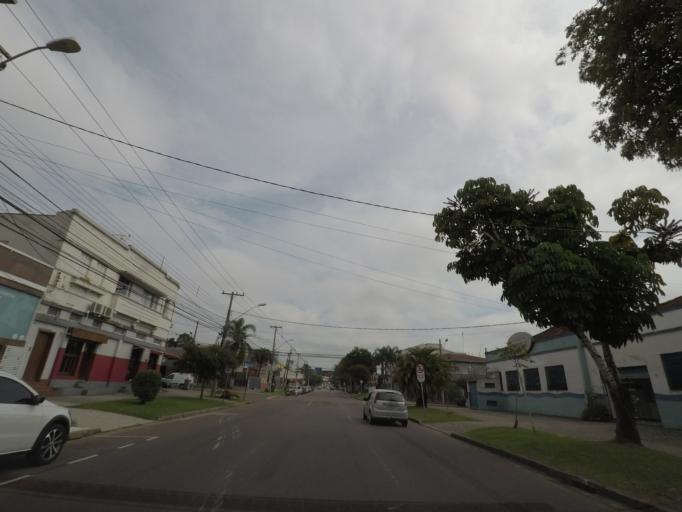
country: BR
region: Parana
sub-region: Curitiba
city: Curitiba
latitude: -25.4518
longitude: -49.2682
